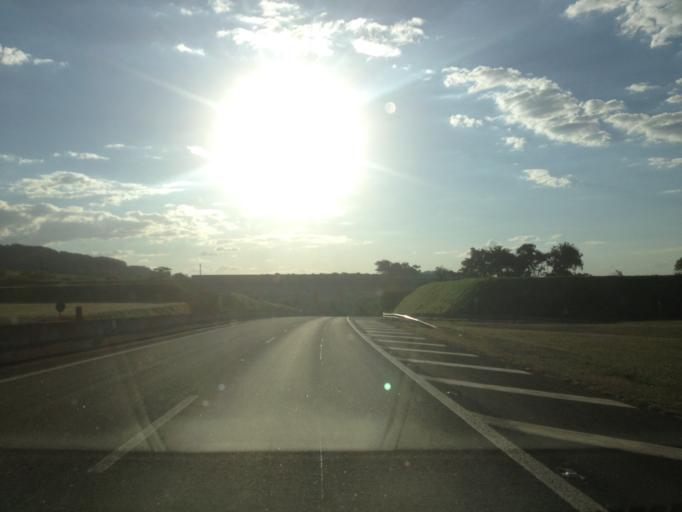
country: BR
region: Sao Paulo
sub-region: Brotas
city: Brotas
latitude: -22.2619
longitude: -48.2363
